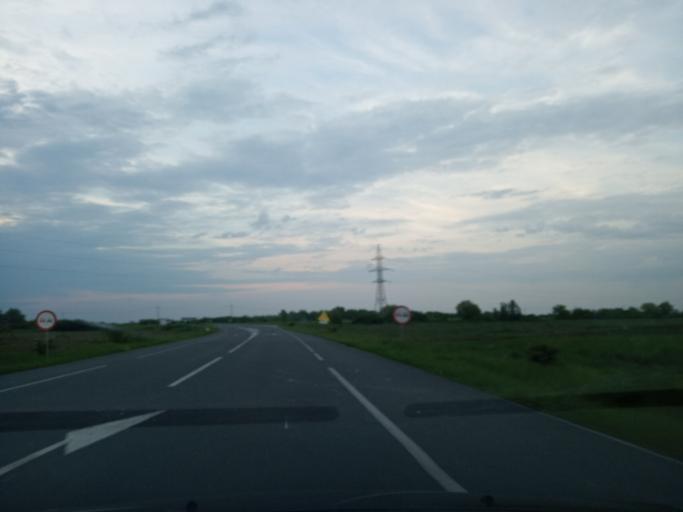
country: RO
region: Timis
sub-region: Oras Deta
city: Deta
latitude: 45.4019
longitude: 21.2388
